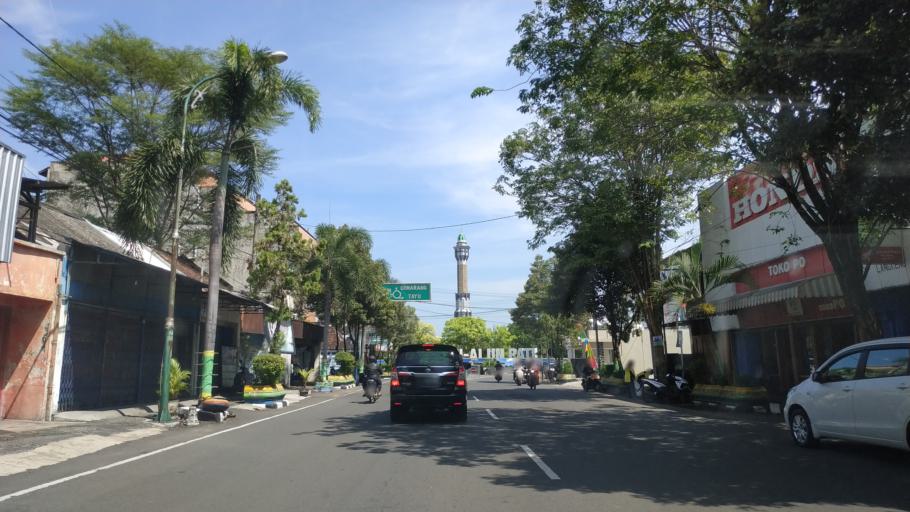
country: ID
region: Central Java
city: Pati
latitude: -6.7537
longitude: 111.0412
